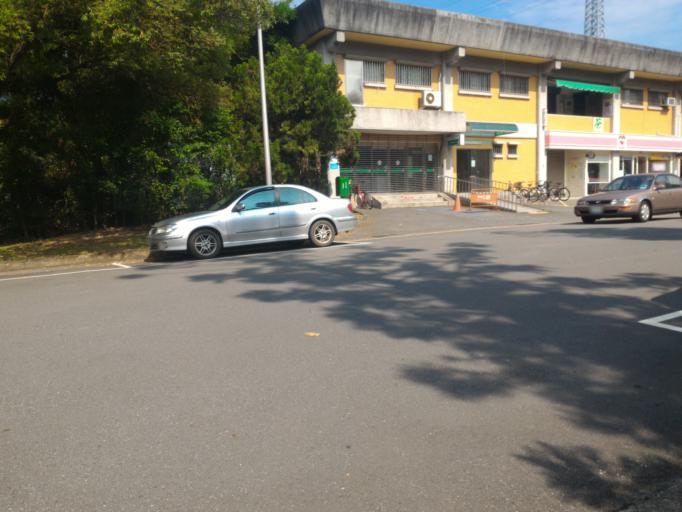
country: TW
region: Taipei
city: Taipei
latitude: 25.0429
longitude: 121.6162
